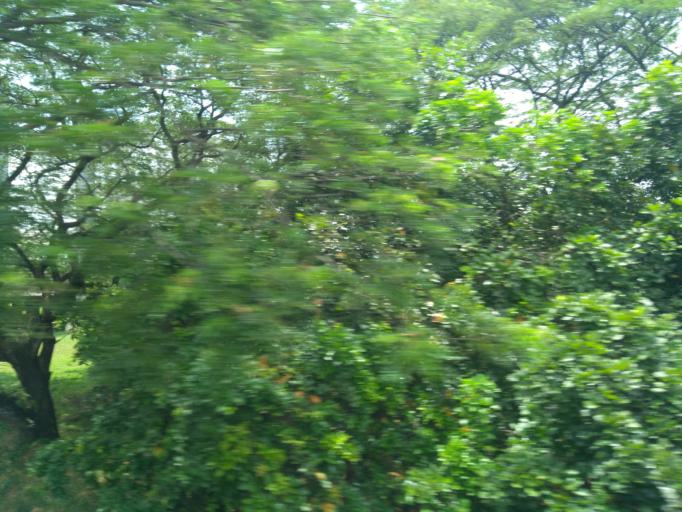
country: MY
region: Penang
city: Perai
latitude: 5.3741
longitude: 100.4027
